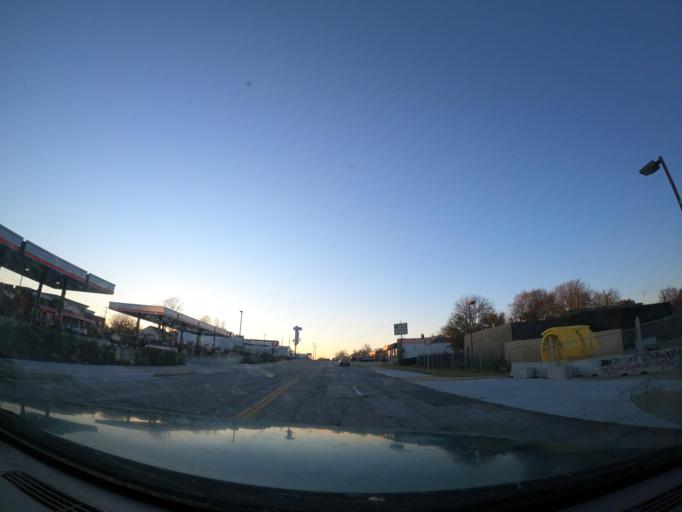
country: US
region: Oklahoma
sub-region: Tulsa County
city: Tulsa
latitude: 36.1608
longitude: -95.9408
